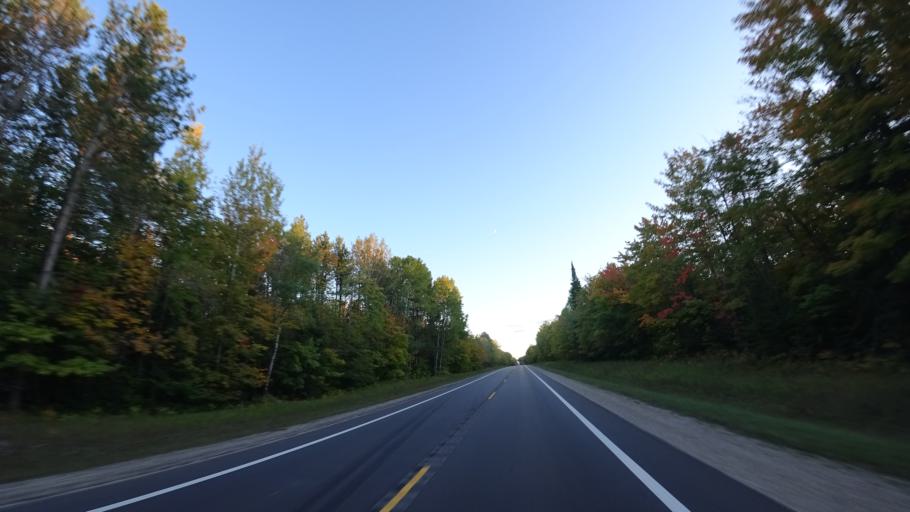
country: US
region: Michigan
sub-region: Luce County
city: Newberry
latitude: 46.2932
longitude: -85.0095
